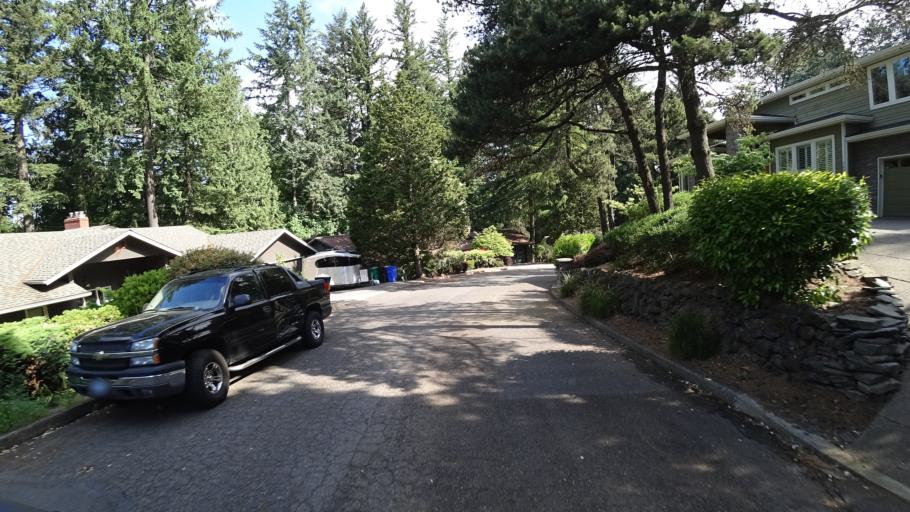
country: US
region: Oregon
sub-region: Washington County
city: West Slope
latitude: 45.5074
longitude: -122.7293
